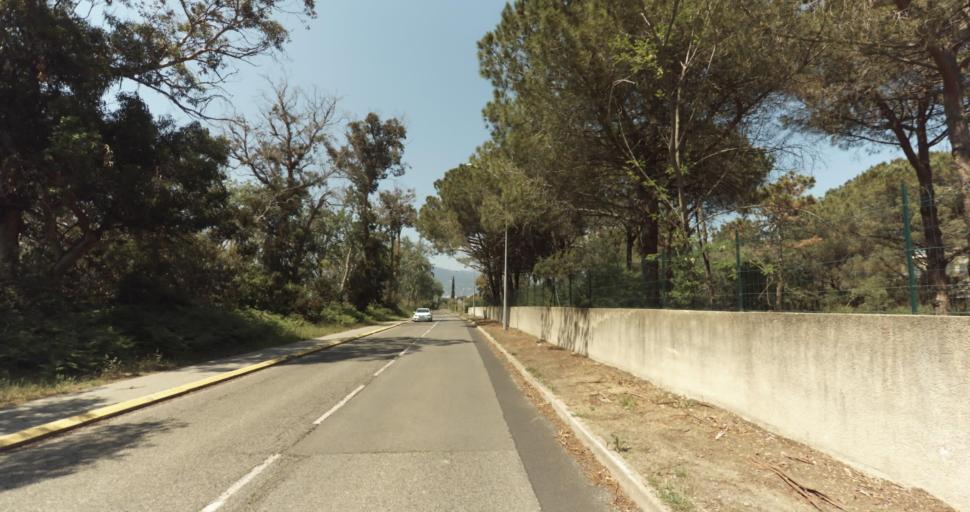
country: FR
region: Corsica
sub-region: Departement de la Haute-Corse
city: Biguglia
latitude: 42.6339
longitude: 9.4632
